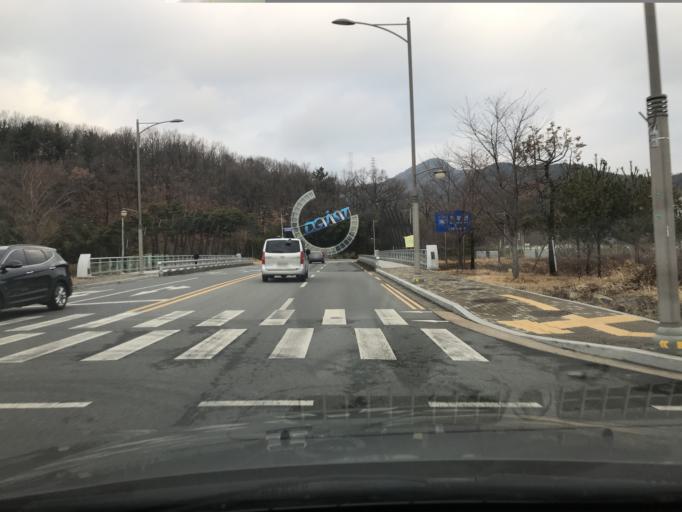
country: KR
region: Daegu
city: Hwawon
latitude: 35.6992
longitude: 128.4578
